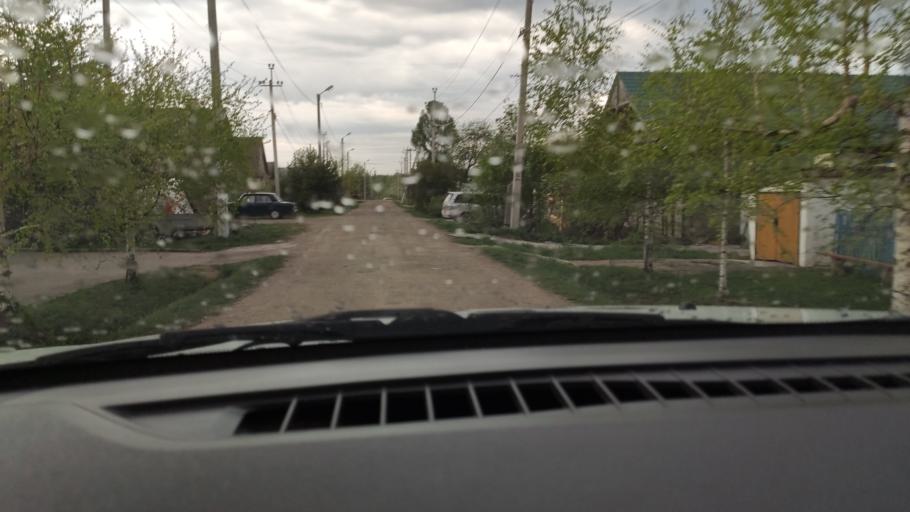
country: RU
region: Perm
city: Froly
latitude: 57.9526
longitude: 56.2897
